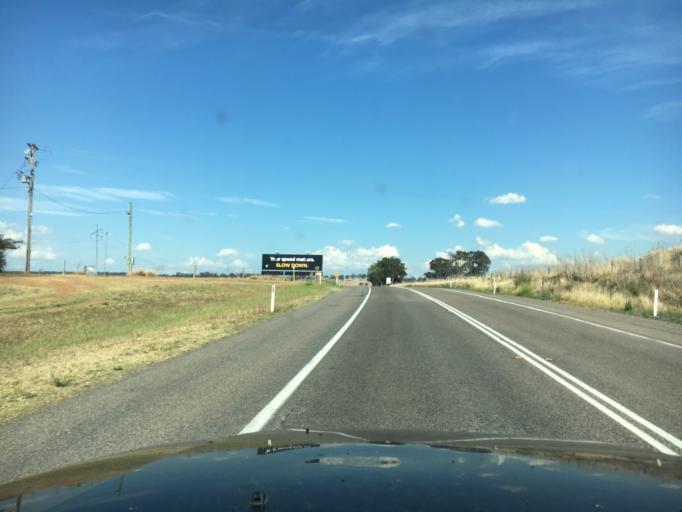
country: AU
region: New South Wales
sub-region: Singleton
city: Singleton
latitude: -32.6173
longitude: 151.2173
